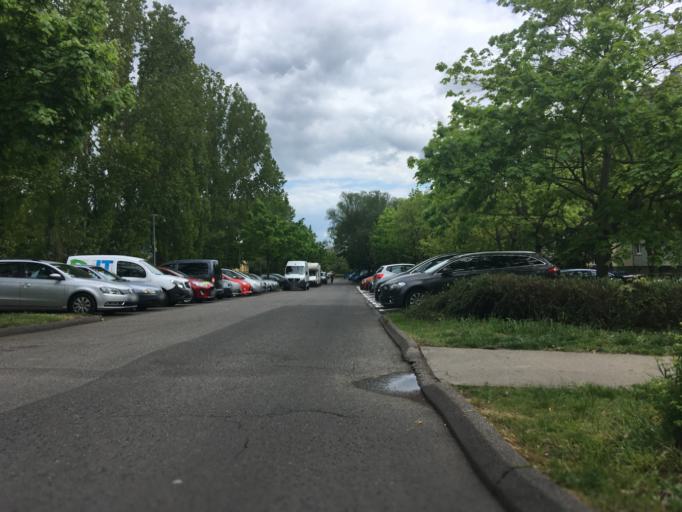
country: DE
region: Berlin
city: Marzahn
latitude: 52.5541
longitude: 13.5782
